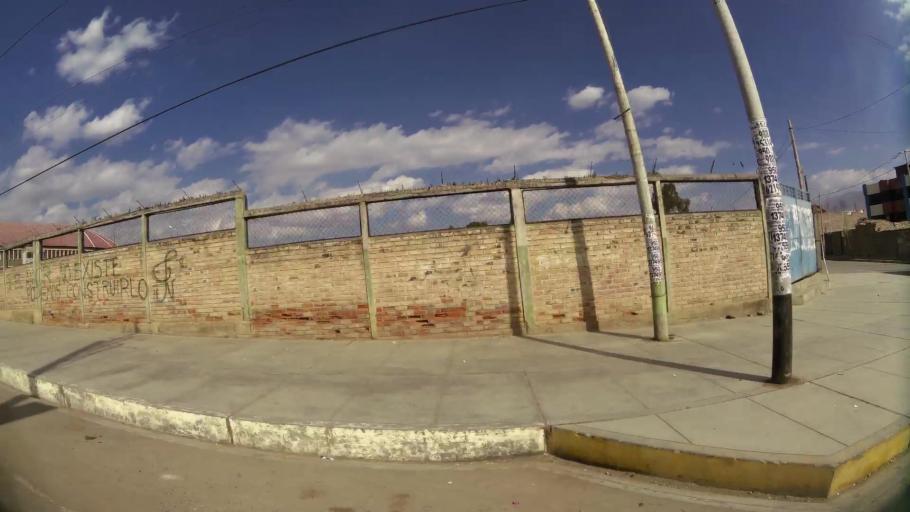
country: PE
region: Junin
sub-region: Provincia de Huancayo
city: El Tambo
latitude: -12.0777
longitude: -75.2119
